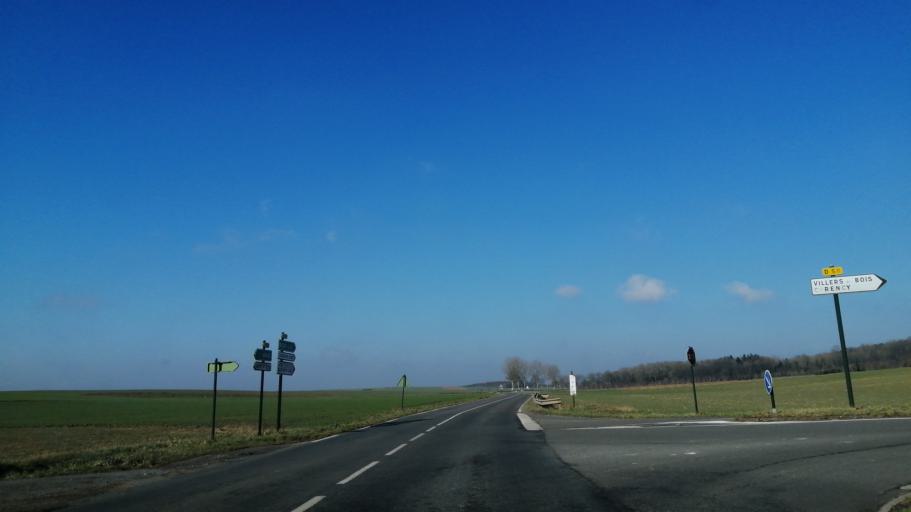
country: FR
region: Nord-Pas-de-Calais
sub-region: Departement du Pas-de-Calais
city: Mont-Saint-Eloi
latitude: 50.3633
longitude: 2.6610
